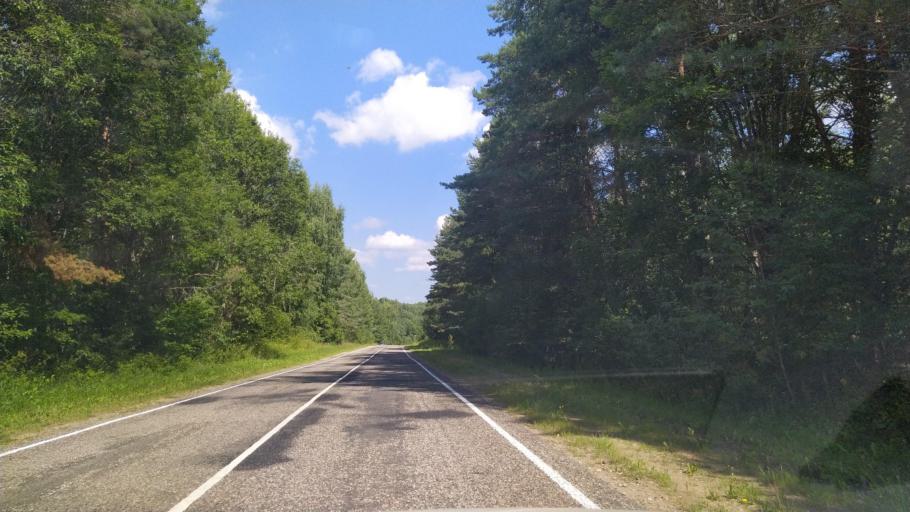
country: RU
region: Pskov
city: Pushkinskiye Gory
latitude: 57.0597
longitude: 28.9472
